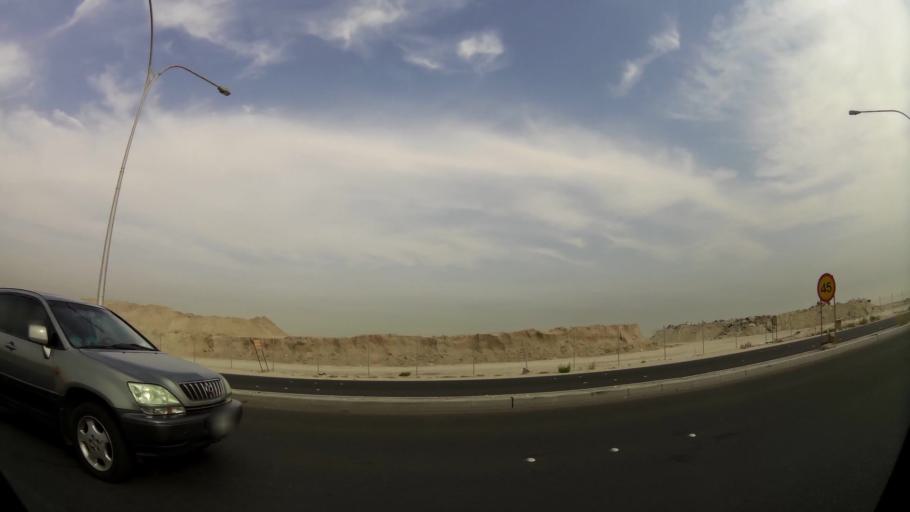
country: KW
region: Al Asimah
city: Ar Rabiyah
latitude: 29.3199
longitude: 47.8369
